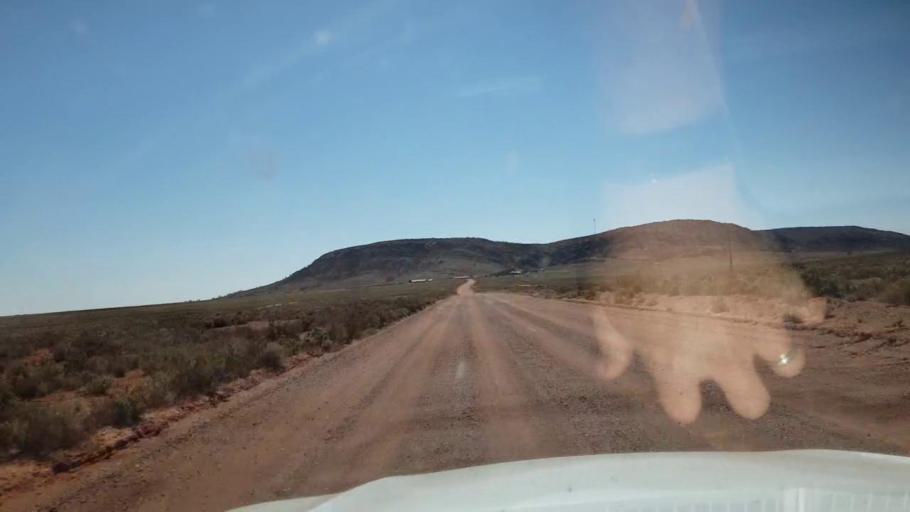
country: AU
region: South Australia
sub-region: Whyalla
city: Whyalla
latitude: -32.6959
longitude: 137.1315
